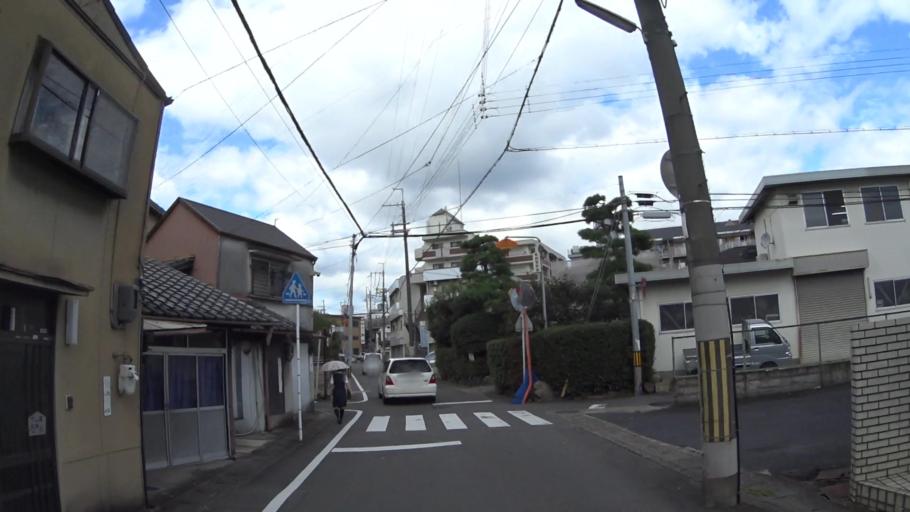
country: JP
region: Shiga Prefecture
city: Otsu-shi
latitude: 34.9798
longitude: 135.8147
